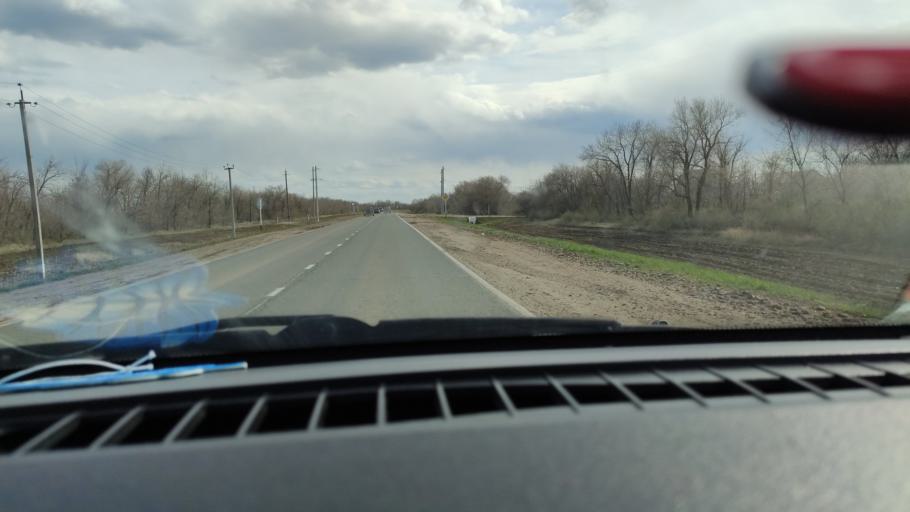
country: RU
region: Saratov
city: Privolzhskiy
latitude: 51.3722
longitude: 46.0462
